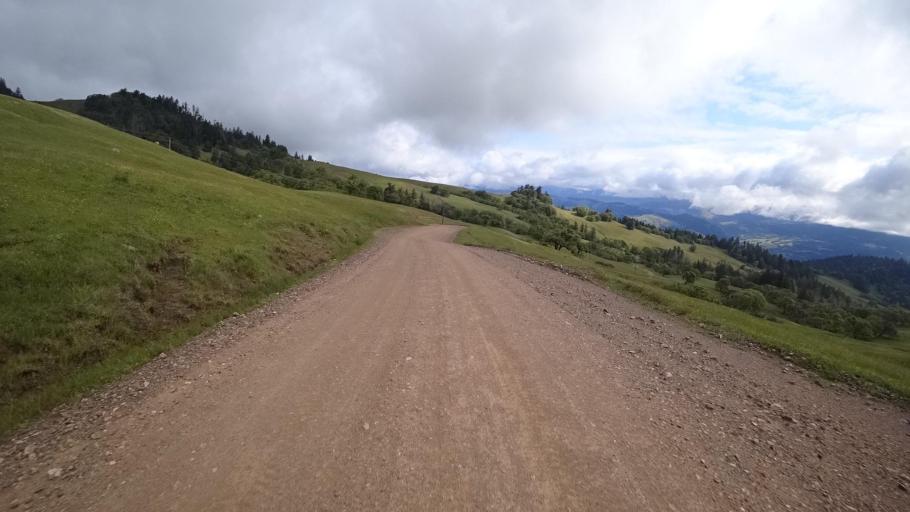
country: US
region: California
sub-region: Humboldt County
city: Redway
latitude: 40.2014
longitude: -123.6937
